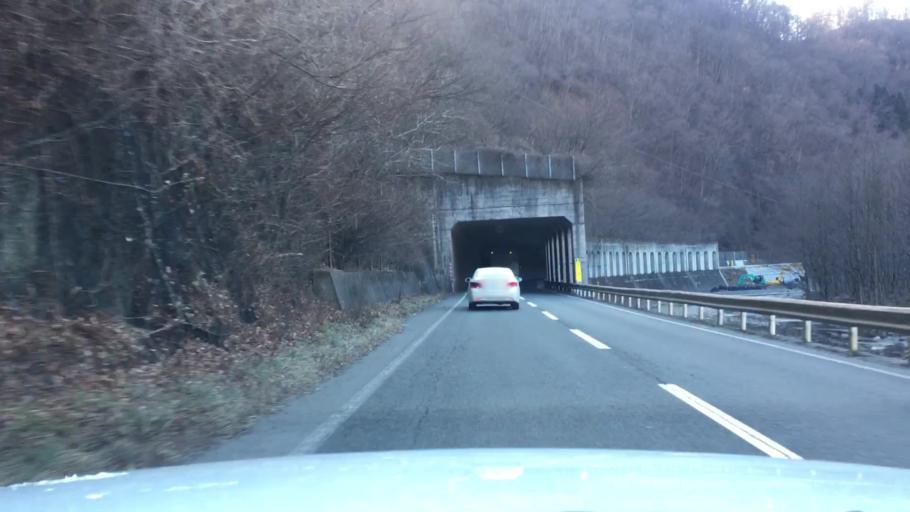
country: JP
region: Iwate
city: Miyako
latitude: 39.6069
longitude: 141.6531
